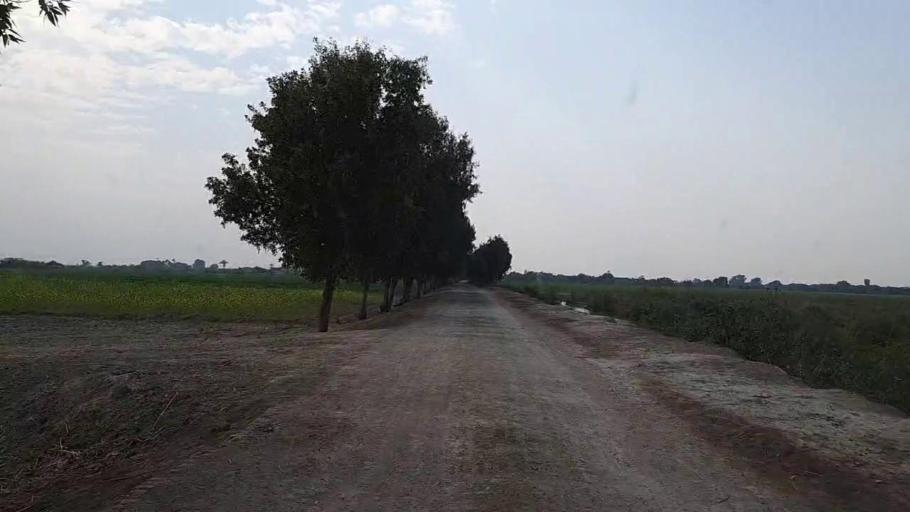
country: PK
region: Sindh
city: Mirwah Gorchani
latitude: 25.3805
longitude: 69.0681
